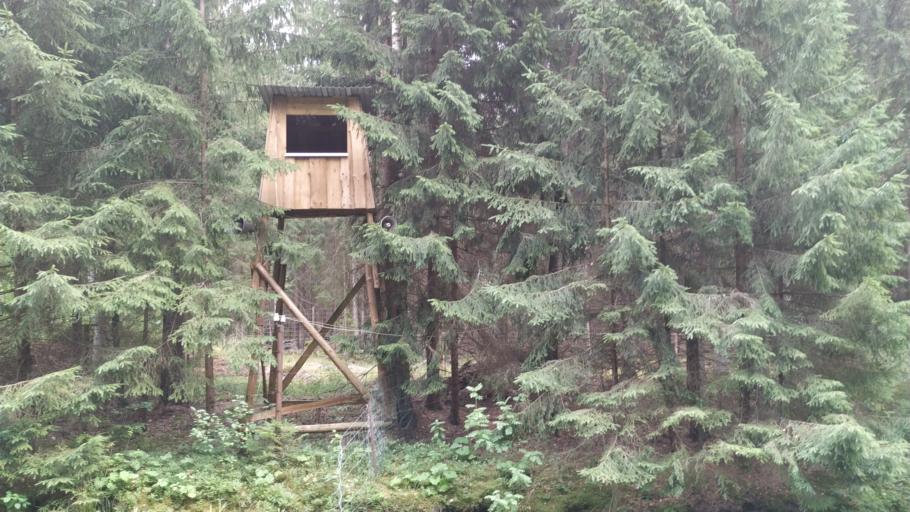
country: LT
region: Alytaus apskritis
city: Druskininkai
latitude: 54.0195
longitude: 24.0789
